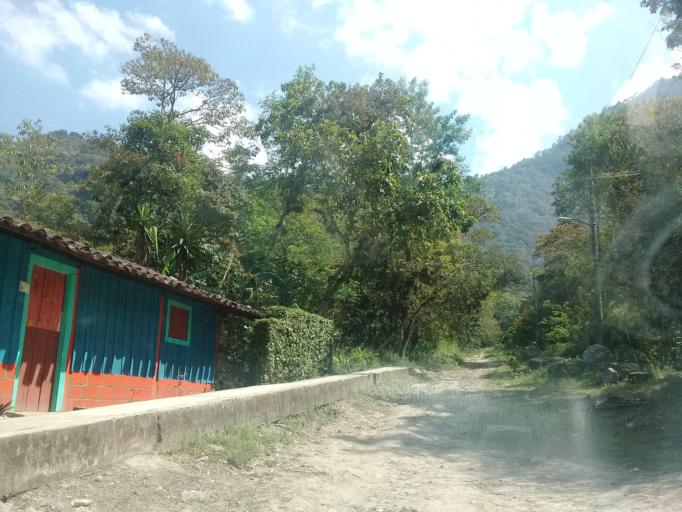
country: MX
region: Veracruz
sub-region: Tlilapan
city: Tonalixco
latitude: 18.8014
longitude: -97.0703
